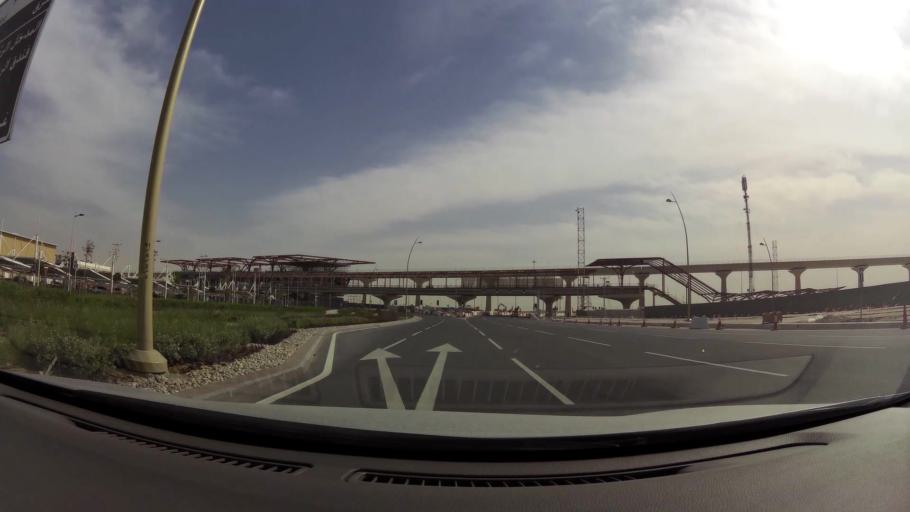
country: QA
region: Baladiyat ar Rayyan
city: Ar Rayyan
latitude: 25.3267
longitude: 51.3470
